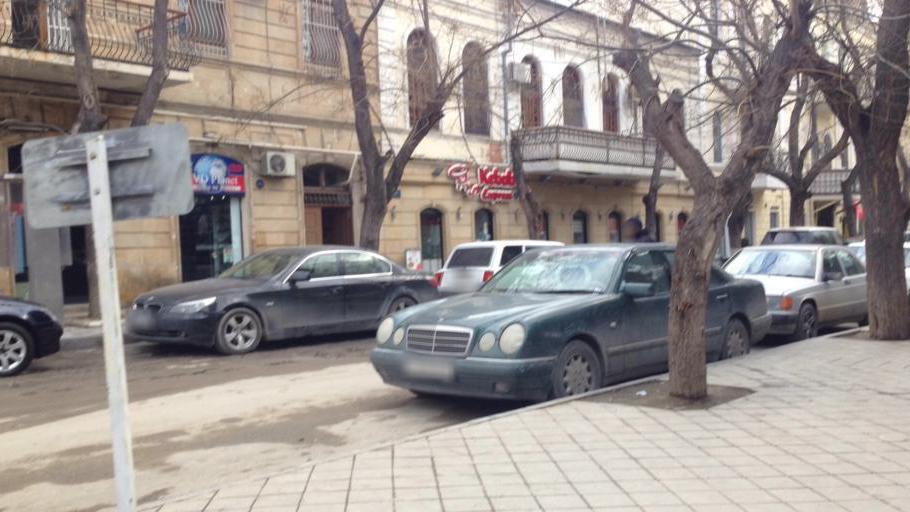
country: AZ
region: Baki
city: Badamdar
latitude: 40.3721
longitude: 49.8405
